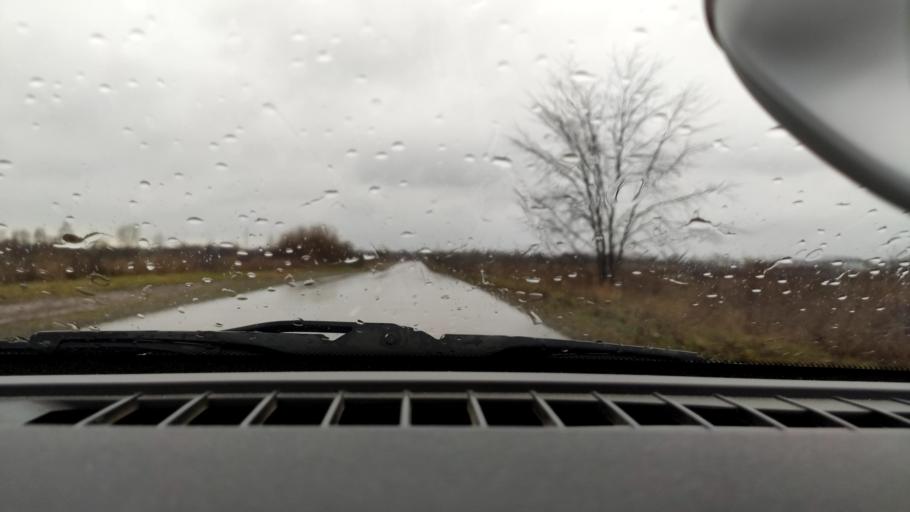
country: RU
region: Perm
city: Kondratovo
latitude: 58.0022
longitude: 56.0660
